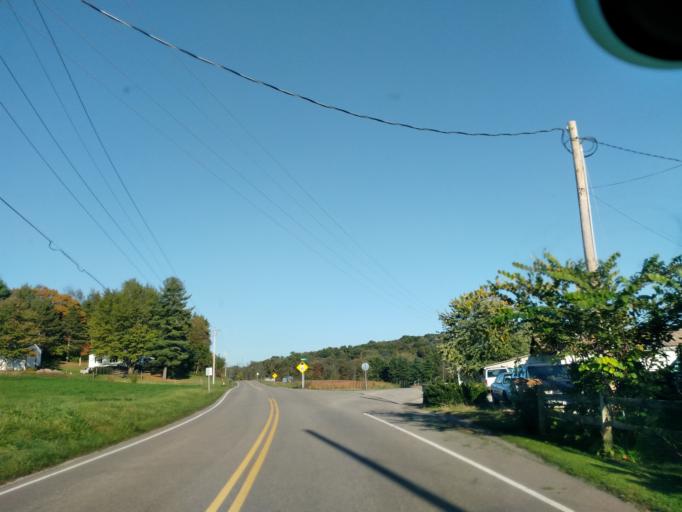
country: US
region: Ohio
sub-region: Fairfield County
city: Lancaster
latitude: 39.6472
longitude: -82.6751
